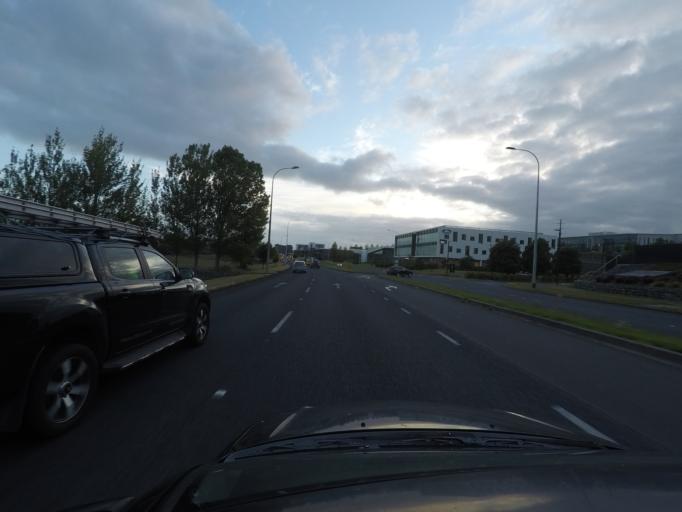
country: NZ
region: Auckland
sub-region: Auckland
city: Tamaki
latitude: -36.9394
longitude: 174.8675
